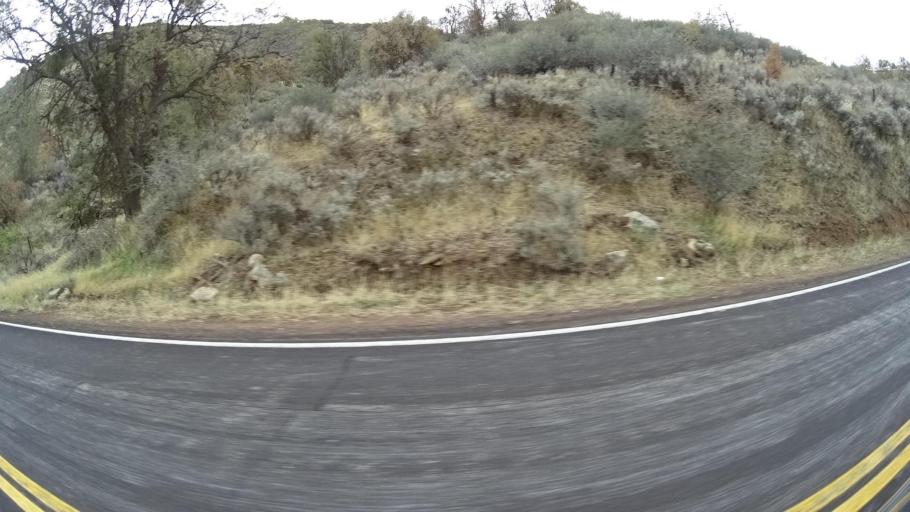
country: US
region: California
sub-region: Kern County
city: Stallion Springs
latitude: 35.0911
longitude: -118.5603
